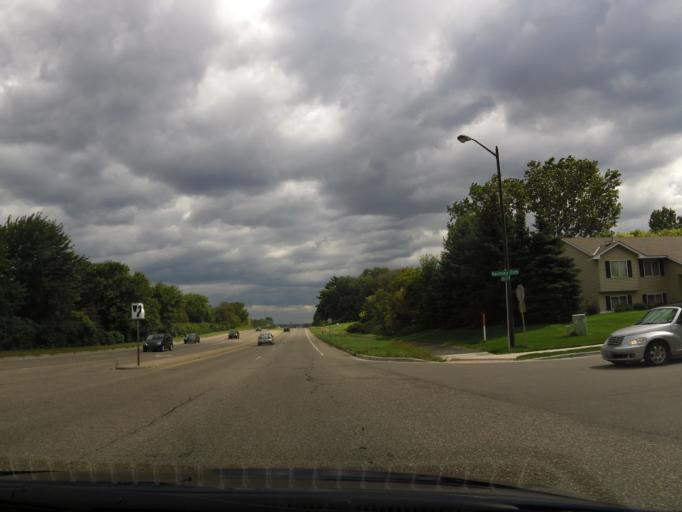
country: US
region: Minnesota
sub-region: Dakota County
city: Apple Valley
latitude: 44.7173
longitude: -93.2307
